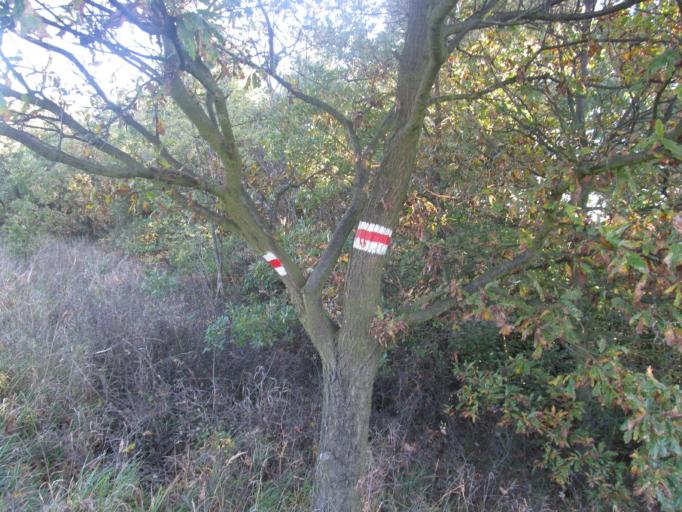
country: HU
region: Gyor-Moson-Sopron
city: Sopron
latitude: 47.7087
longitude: 16.5767
